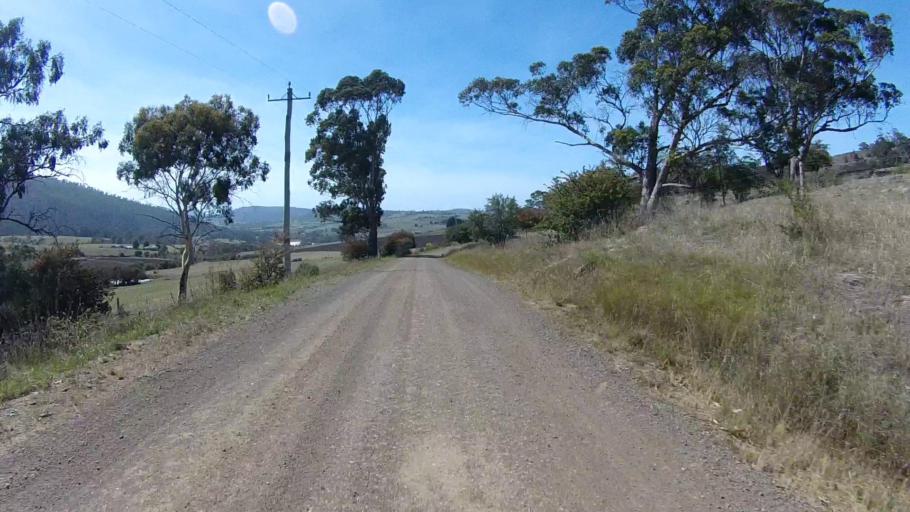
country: AU
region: Tasmania
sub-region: Sorell
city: Sorell
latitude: -42.7438
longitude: 147.6015
